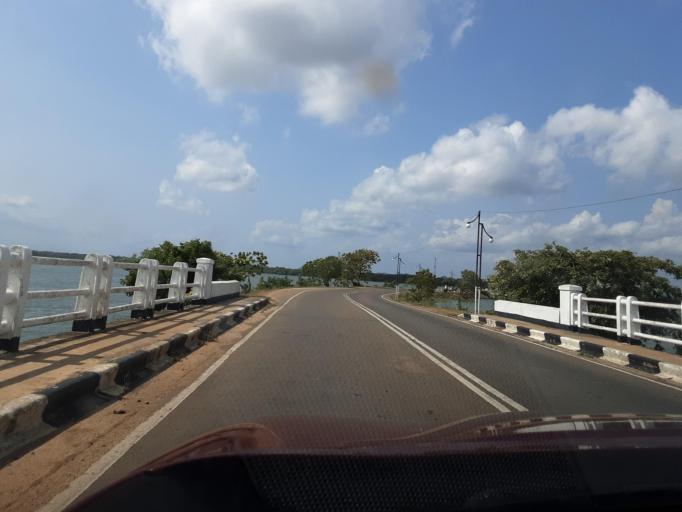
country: LK
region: Southern
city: Tangalla
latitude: 6.2855
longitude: 81.2318
